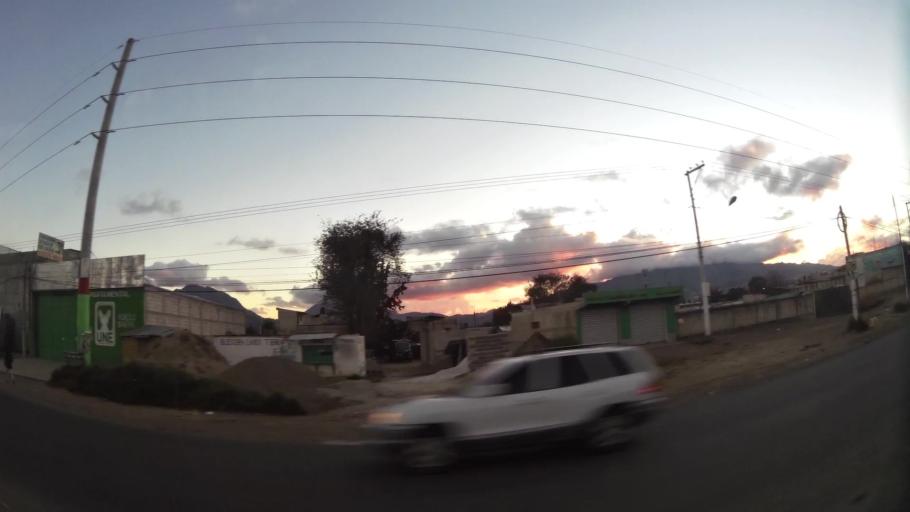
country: GT
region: Quetzaltenango
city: Olintepeque
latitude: 14.8612
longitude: -91.5251
